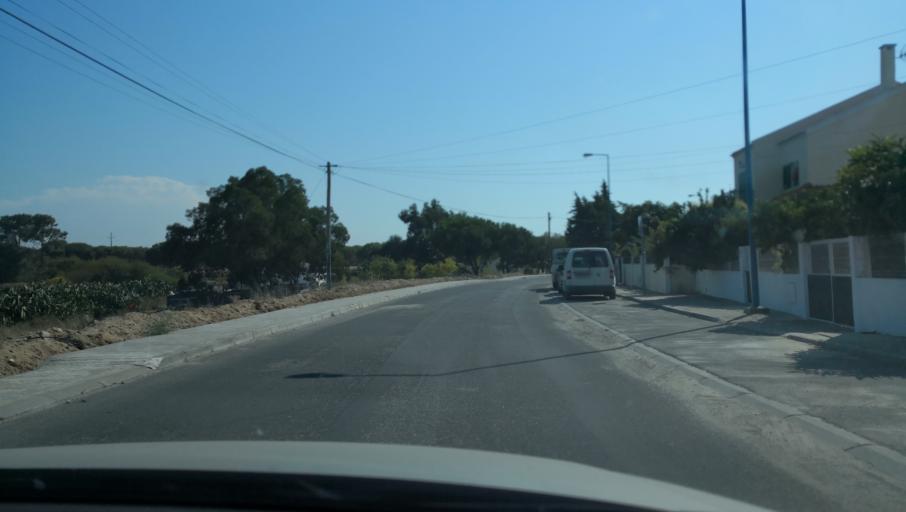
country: PT
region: Setubal
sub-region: Setubal
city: Setubal
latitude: 38.4069
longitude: -8.7522
